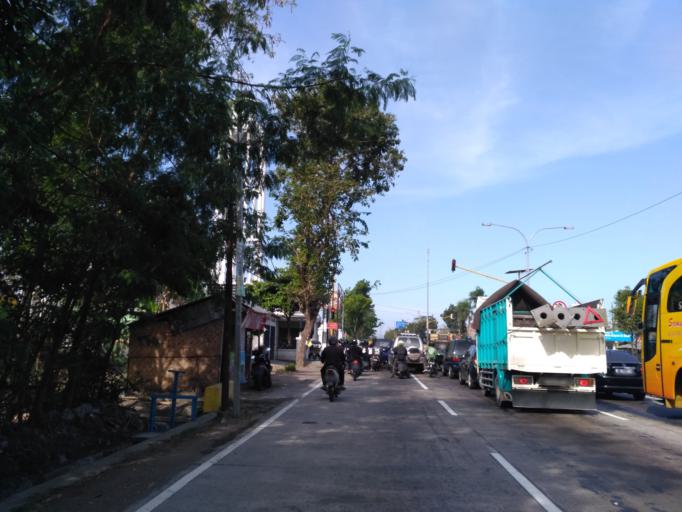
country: ID
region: Daerah Istimewa Yogyakarta
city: Kasihan
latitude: -7.8264
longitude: 110.3444
